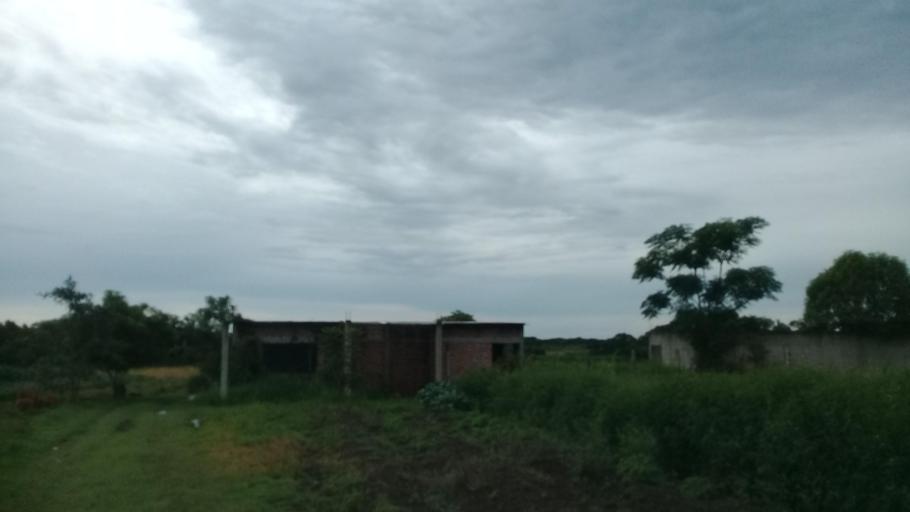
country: MX
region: Veracruz
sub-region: Emiliano Zapata
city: Dos Rios
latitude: 19.4786
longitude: -96.8102
